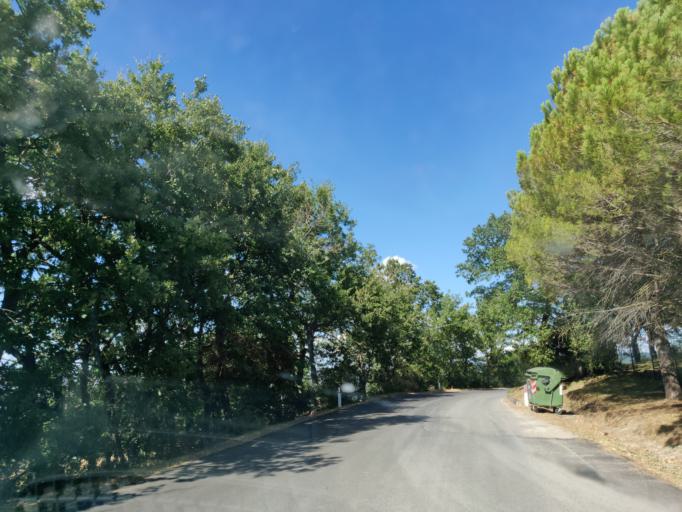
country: IT
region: Tuscany
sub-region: Provincia di Siena
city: Radicofani
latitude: 42.9643
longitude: 11.7293
